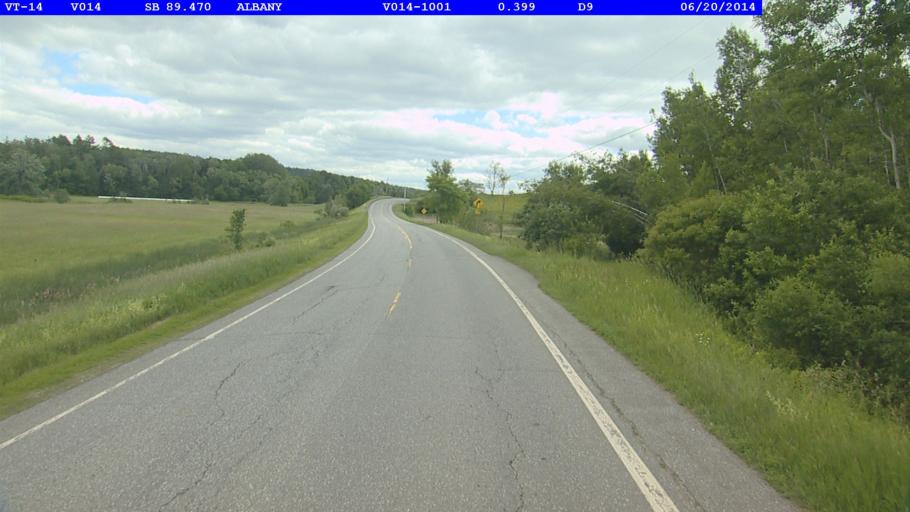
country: US
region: Vermont
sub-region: Caledonia County
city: Hardwick
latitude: 44.7083
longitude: -72.3897
